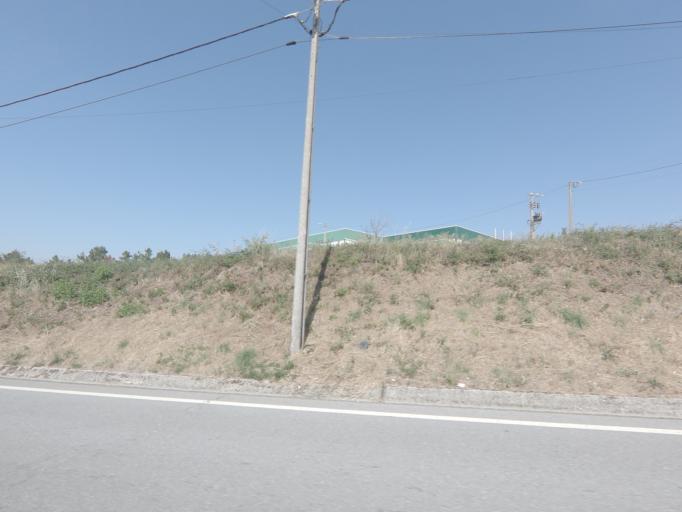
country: PT
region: Viseu
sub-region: Tarouca
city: Tarouca
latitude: 41.0077
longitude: -7.7004
